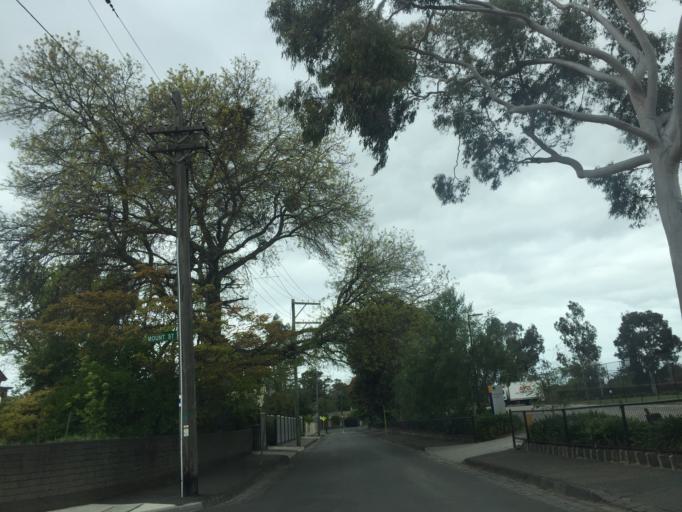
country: AU
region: Victoria
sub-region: Boroondara
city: Hawthorn East
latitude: -37.8149
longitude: 145.0494
